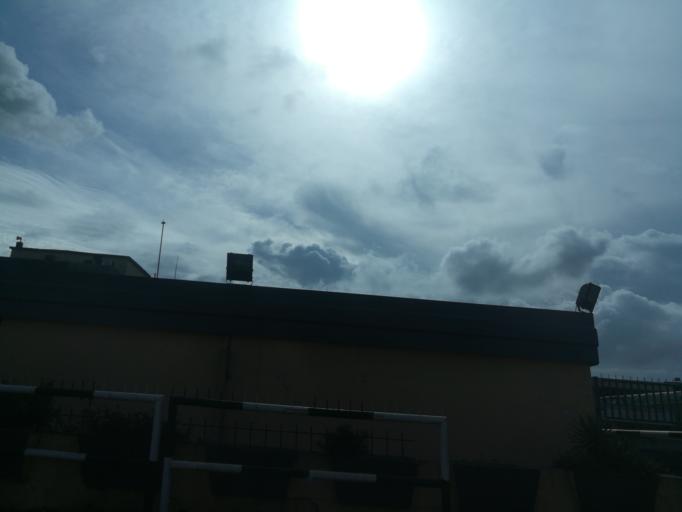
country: NG
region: Lagos
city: Ikeja
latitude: 6.6218
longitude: 3.3526
